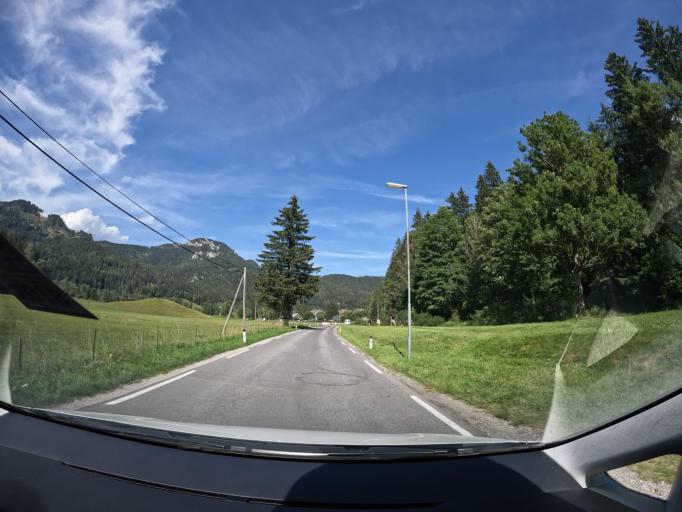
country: AT
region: Carinthia
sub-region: Politischer Bezirk Feldkirchen
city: Feldkirchen in Karnten
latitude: 46.7058
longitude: 14.1269
